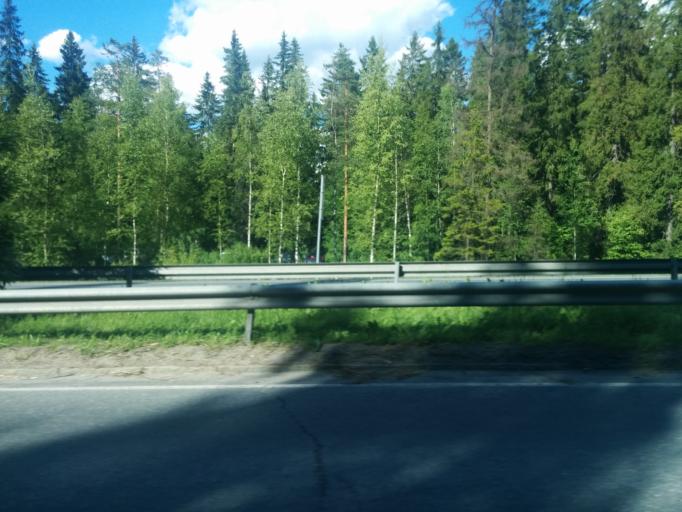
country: FI
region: Pirkanmaa
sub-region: Tampere
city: Tampere
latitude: 61.5020
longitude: 23.8668
